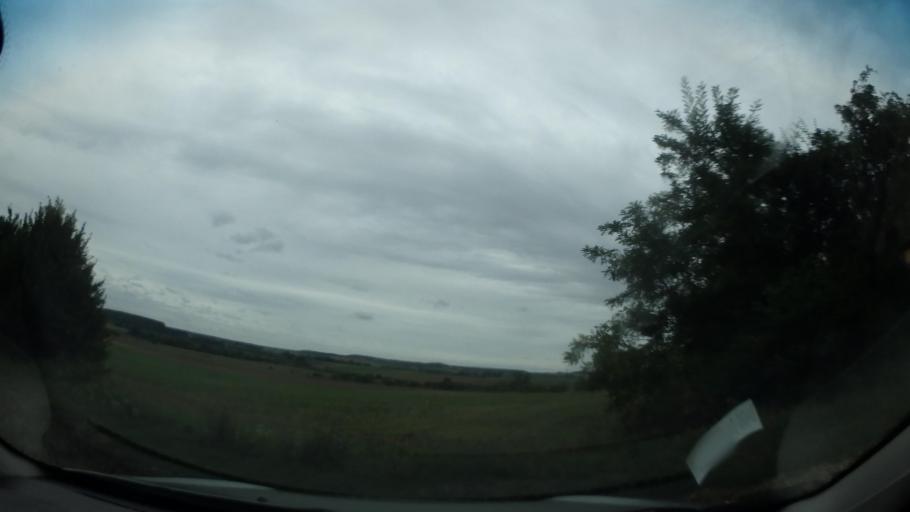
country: CZ
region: Central Bohemia
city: Lysa nad Labem
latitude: 50.2138
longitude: 14.8541
